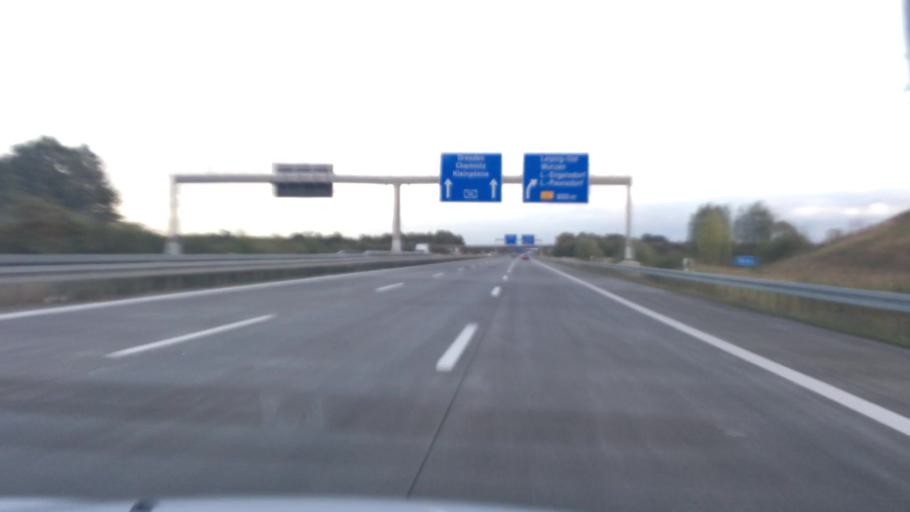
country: DE
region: Saxony
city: Taucha
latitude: 51.3612
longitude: 12.4836
